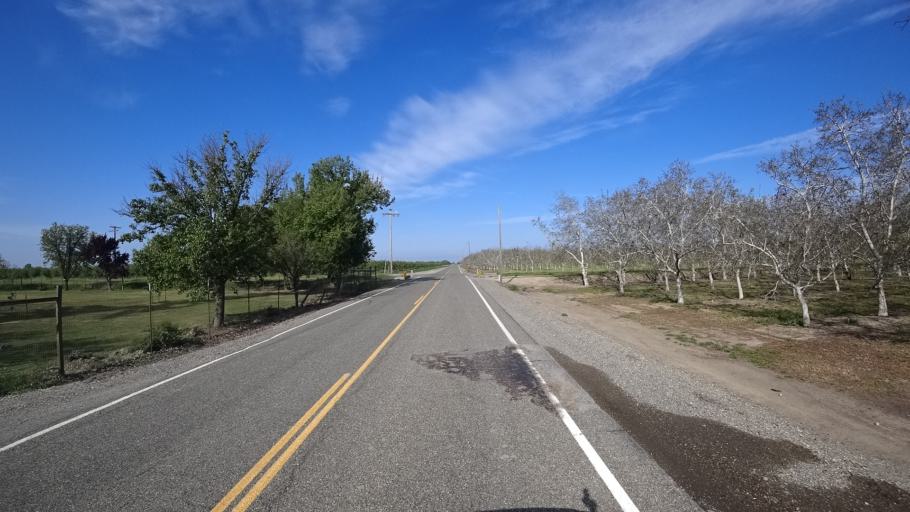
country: US
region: California
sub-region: Glenn County
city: Hamilton City
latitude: 39.6306
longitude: -122.0267
